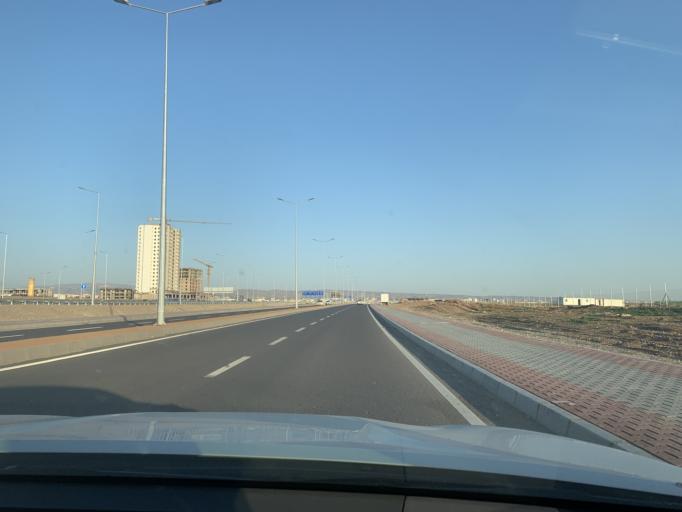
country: IQ
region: Arbil
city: Erbil
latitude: 36.2874
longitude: 44.0363
